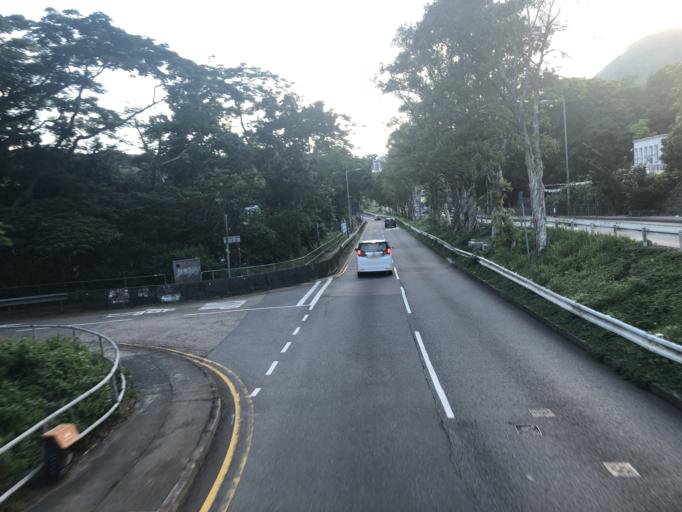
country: HK
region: Sai Kung
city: Sai Kung
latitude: 22.3348
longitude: 114.2407
